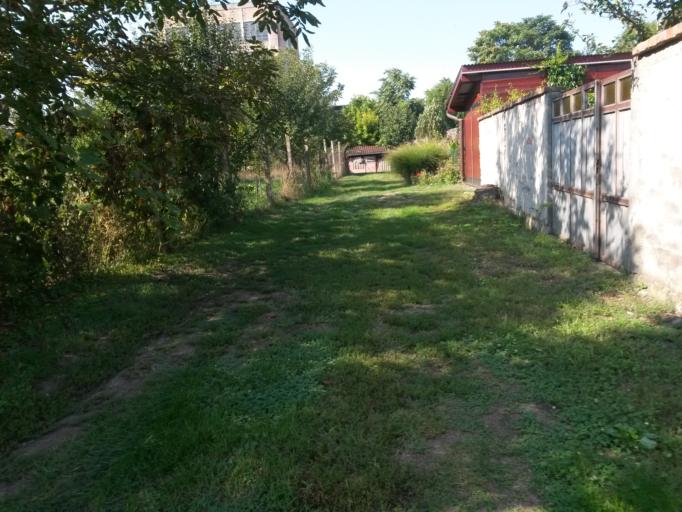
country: HR
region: Osjecko-Baranjska
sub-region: Grad Osijek
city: Osijek
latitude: 45.5501
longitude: 18.6767
